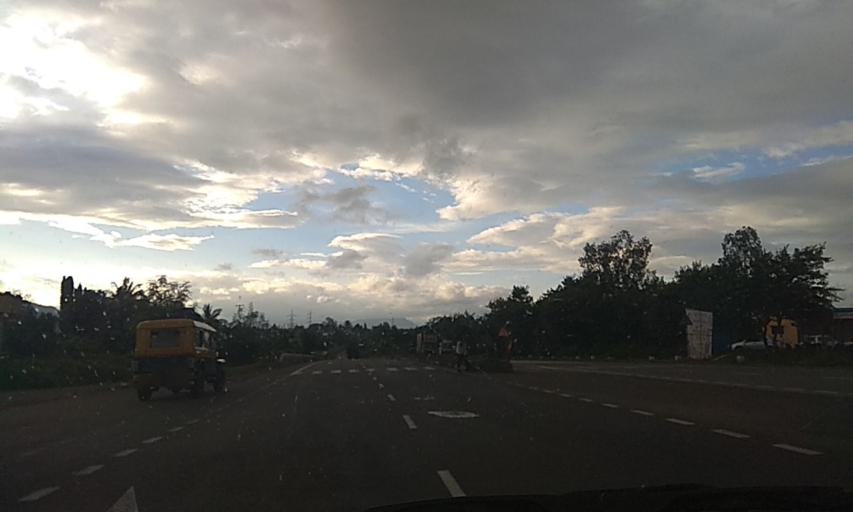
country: IN
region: Maharashtra
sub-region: Satara Division
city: Rahimatpur
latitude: 17.5261
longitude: 74.0690
